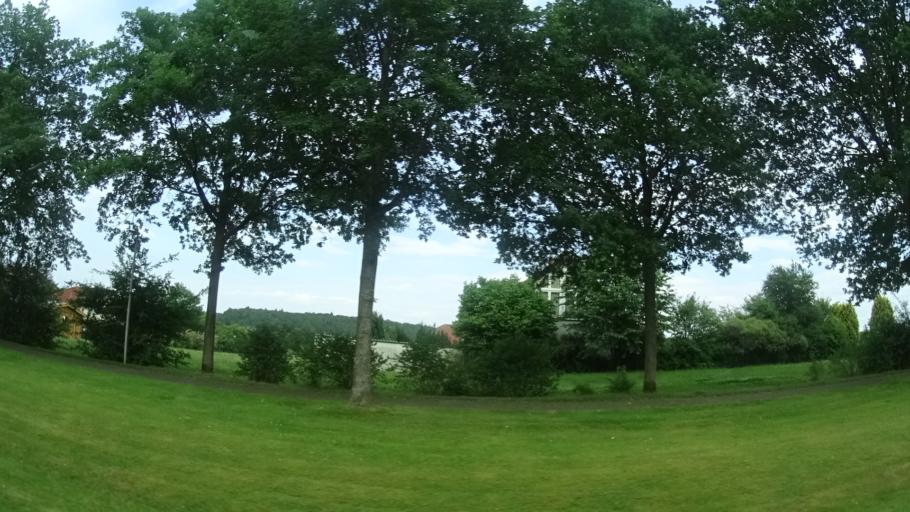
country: DE
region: Hesse
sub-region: Regierungsbezirk Kassel
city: Bad Arolsen
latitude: 51.3786
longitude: 9.0557
